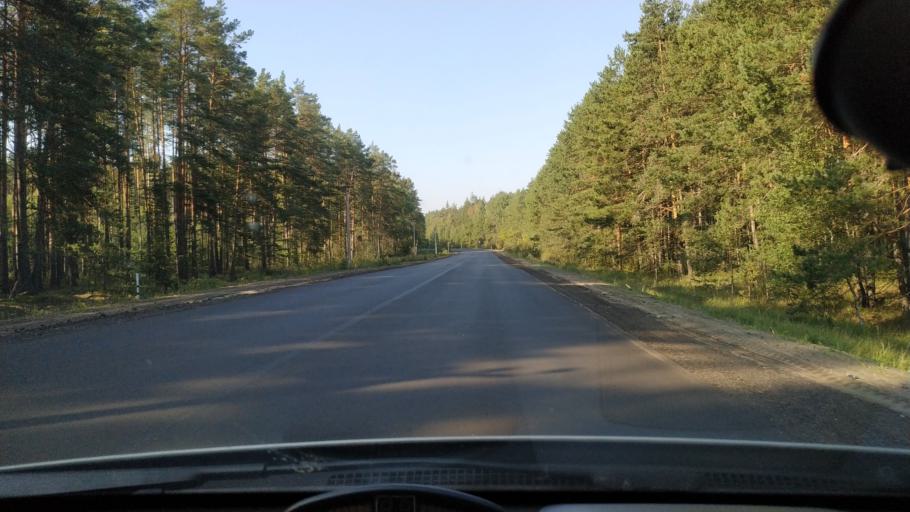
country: RU
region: Moskovskaya
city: Misheronskiy
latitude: 55.6263
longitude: 39.7373
